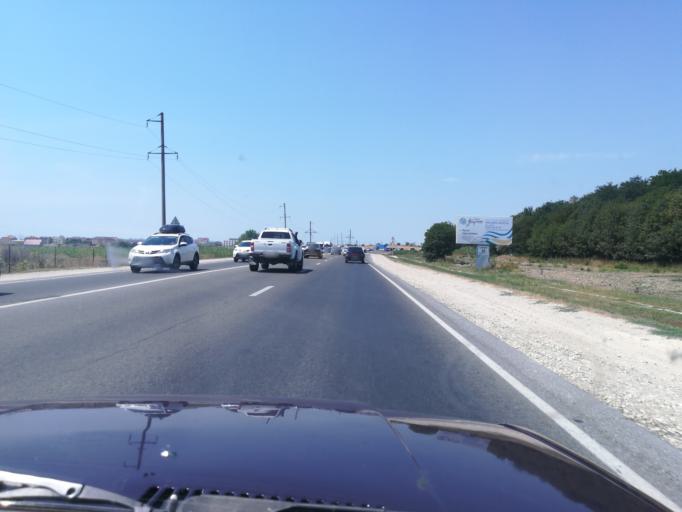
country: RU
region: Krasnodarskiy
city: Tsibanobalka
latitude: 44.9564
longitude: 37.3089
